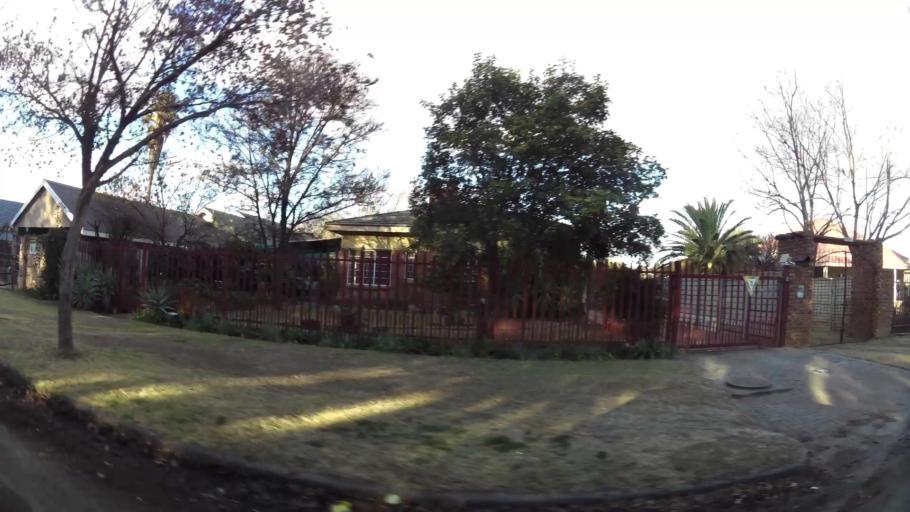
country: ZA
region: North-West
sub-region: Dr Kenneth Kaunda District Municipality
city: Potchefstroom
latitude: -26.7255
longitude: 27.0846
